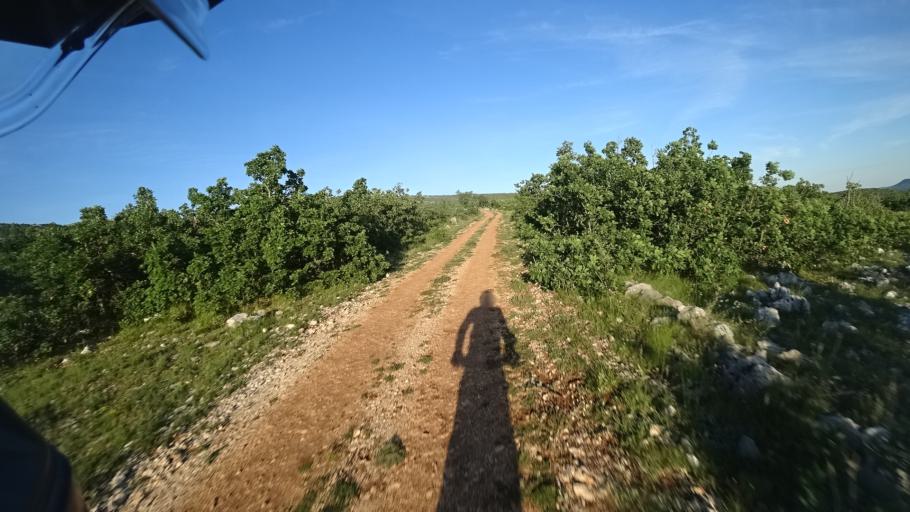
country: HR
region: Sibensko-Kniniska
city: Drnis
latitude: 43.8514
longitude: 16.3493
